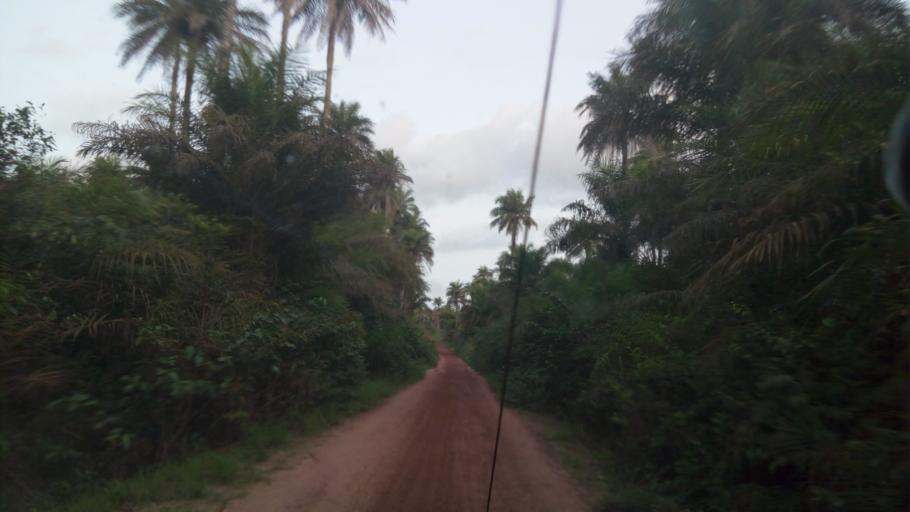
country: SL
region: Northern Province
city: Mambolo
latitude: 8.9877
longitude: -13.0040
